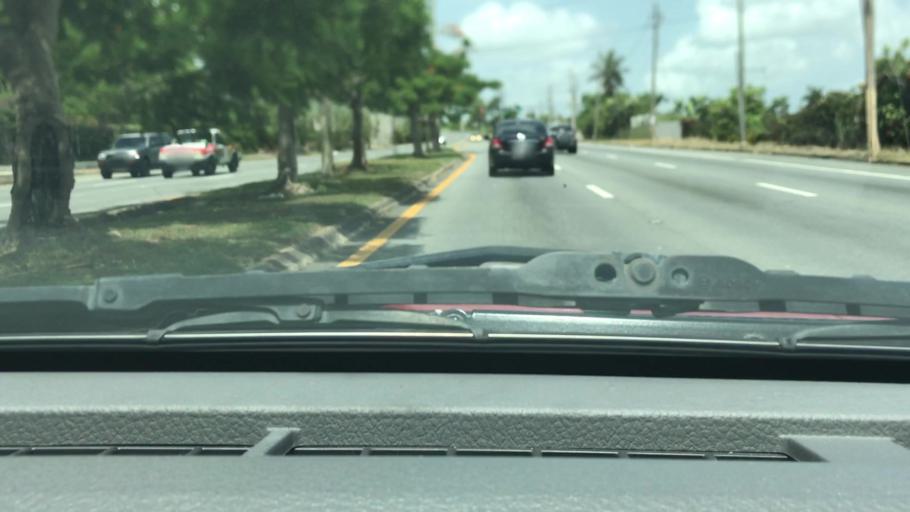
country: PR
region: Toa Alta
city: Pajaros
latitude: 18.3645
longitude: -66.1811
